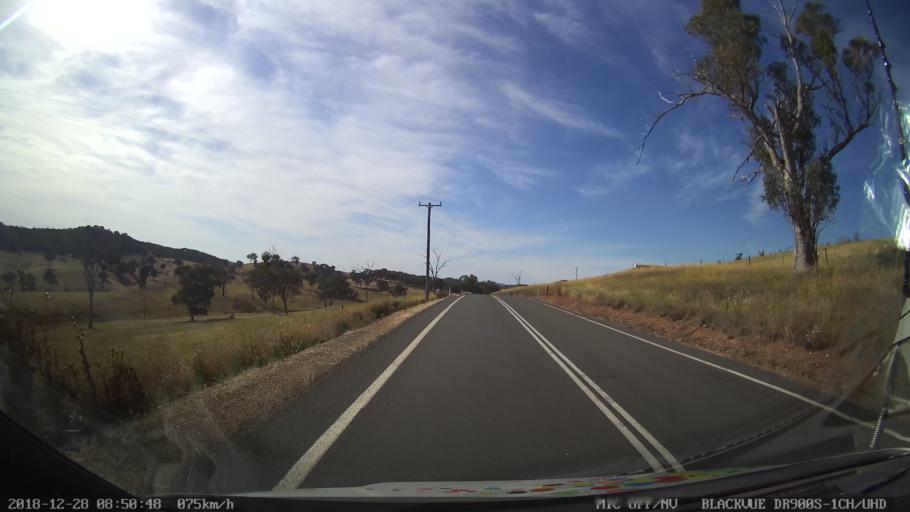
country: AU
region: New South Wales
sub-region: Upper Lachlan Shire
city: Crookwell
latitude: -34.0623
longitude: 149.3387
